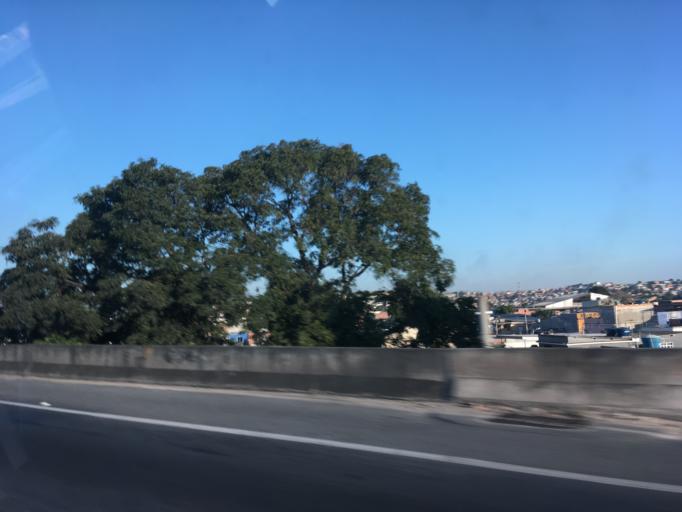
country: BR
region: Rio de Janeiro
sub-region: Belford Roxo
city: Belford Roxo
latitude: -22.7826
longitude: -43.3868
